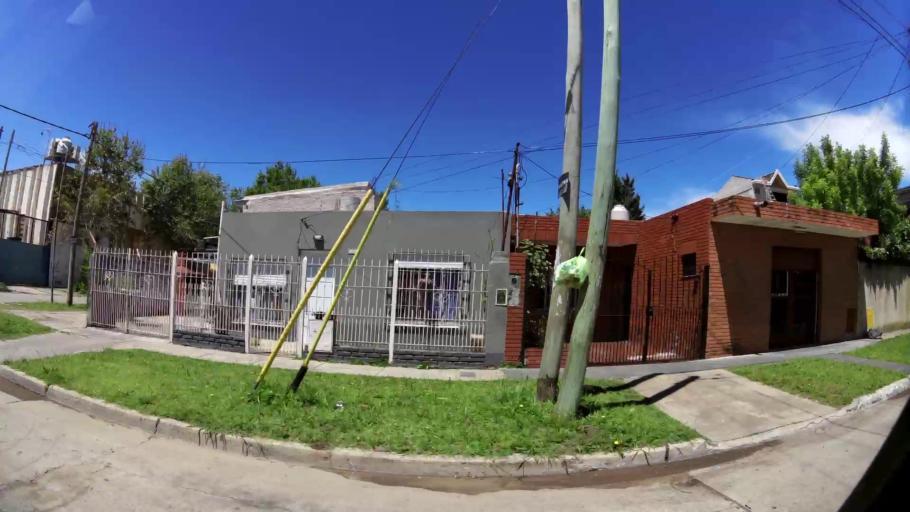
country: AR
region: Buenos Aires
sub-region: Partido de Quilmes
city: Quilmes
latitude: -34.7424
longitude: -58.2753
